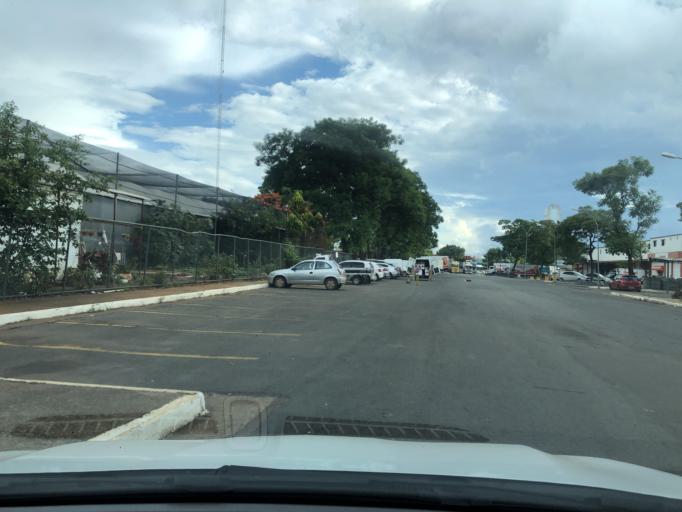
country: BR
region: Federal District
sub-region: Brasilia
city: Brasilia
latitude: -15.7932
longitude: -47.9499
